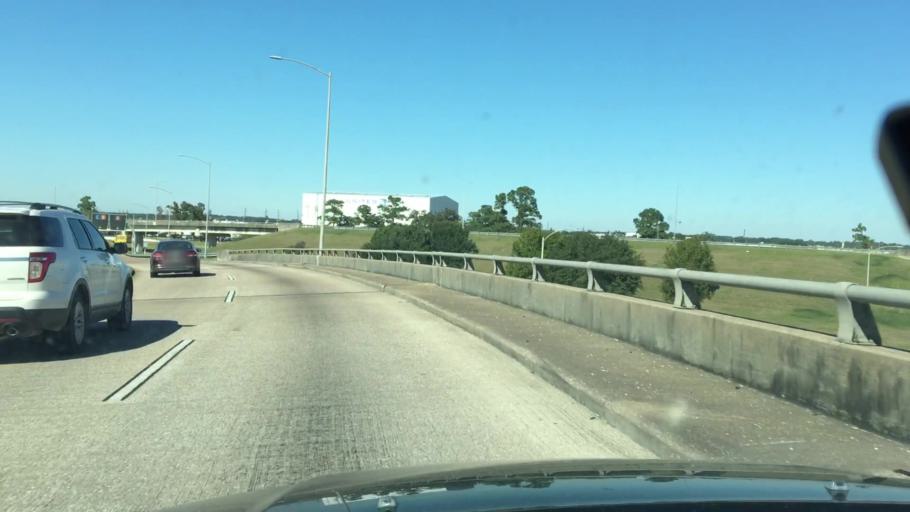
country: US
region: Texas
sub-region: Harris County
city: Humble
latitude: 29.9833
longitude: -95.3259
